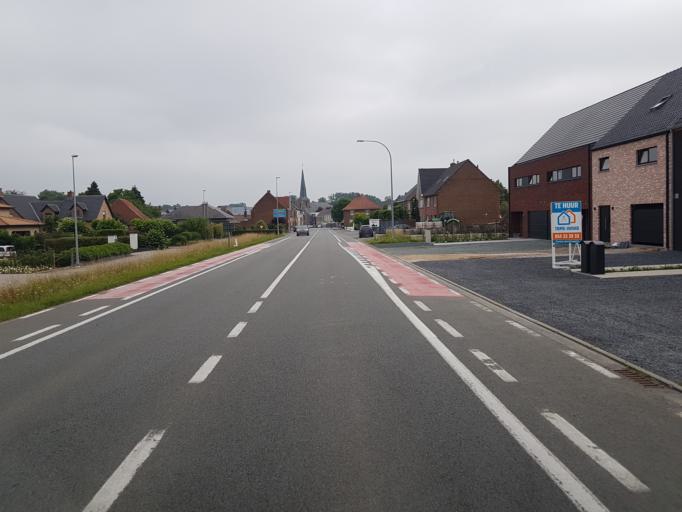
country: BE
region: Flanders
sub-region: Provincie Oost-Vlaanderen
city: Ninove
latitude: 50.8396
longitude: 3.9537
